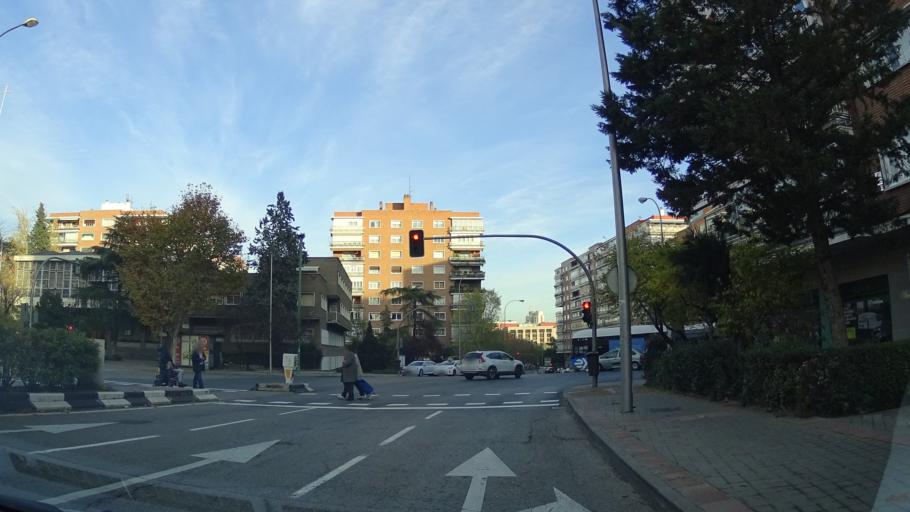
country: ES
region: Madrid
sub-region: Provincia de Madrid
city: Salamanca
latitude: 40.4411
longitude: -3.6633
